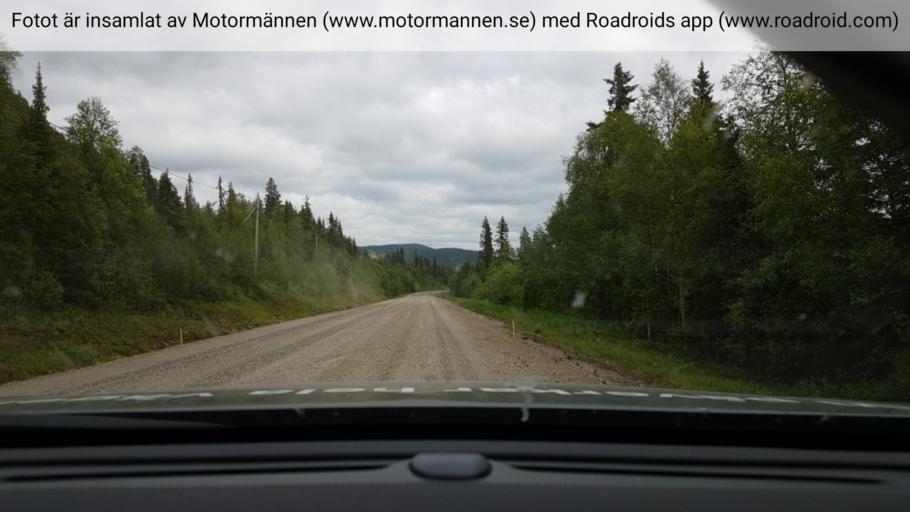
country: SE
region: Vaesterbotten
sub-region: Storumans Kommun
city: Fristad
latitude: 65.8163
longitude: 16.7737
